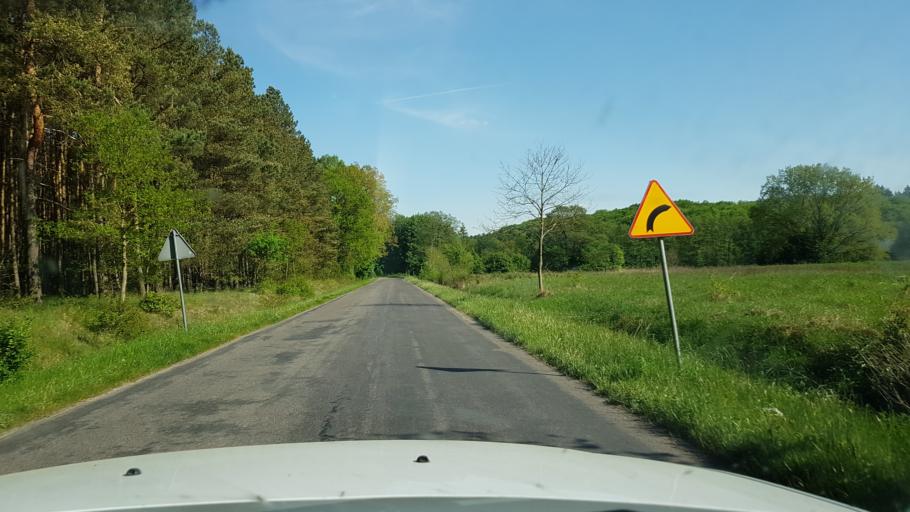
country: PL
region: West Pomeranian Voivodeship
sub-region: Powiat lobeski
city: Resko
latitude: 53.8435
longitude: 15.3701
